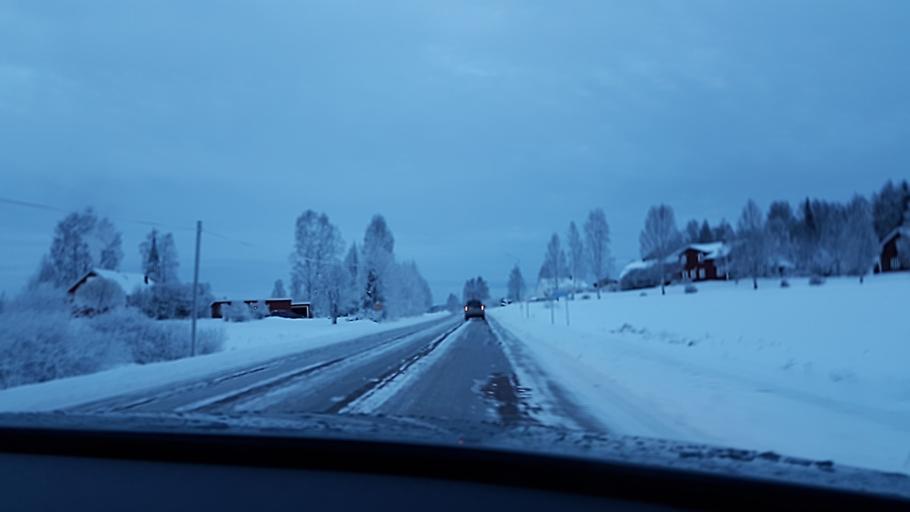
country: SE
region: Jaemtland
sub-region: Harjedalens Kommun
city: Sveg
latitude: 62.0439
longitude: 14.6664
